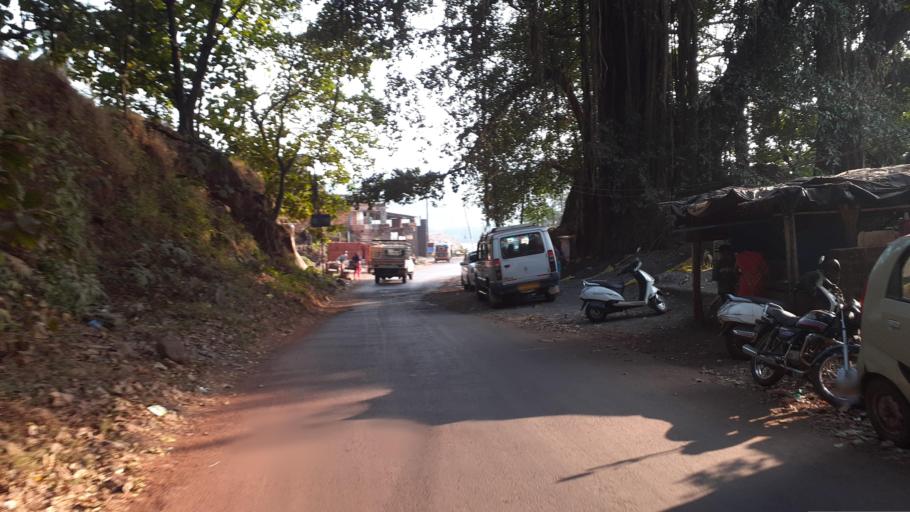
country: IN
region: Maharashtra
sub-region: Ratnagiri
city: Ratnagiri
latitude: 17.0426
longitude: 73.2979
